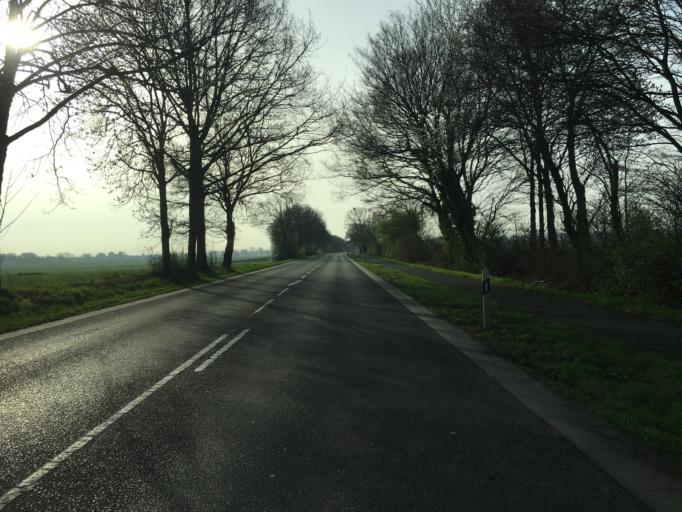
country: DE
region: North Rhine-Westphalia
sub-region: Regierungsbezirk Koln
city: Hurth
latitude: 50.8967
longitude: 6.8465
